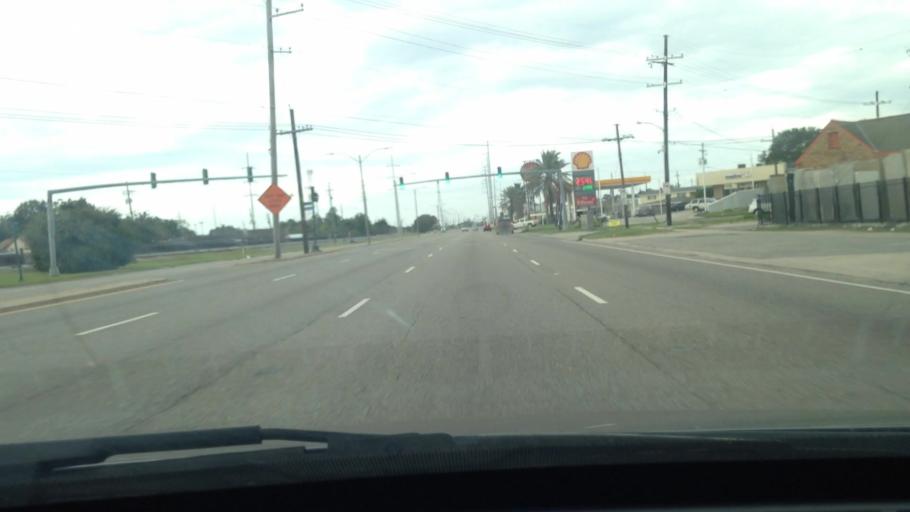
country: US
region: Louisiana
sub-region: Jefferson Parish
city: Jefferson
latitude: 29.9718
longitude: -90.1197
